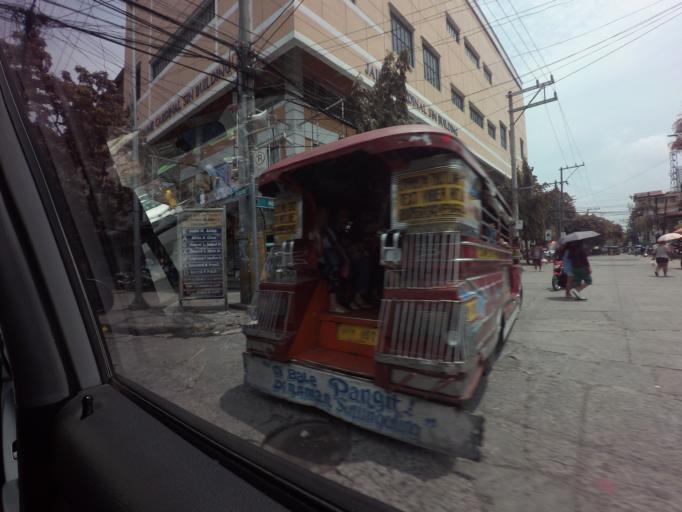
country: PH
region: Metro Manila
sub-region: City of Manila
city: Quiapo
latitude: 14.5788
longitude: 120.9952
